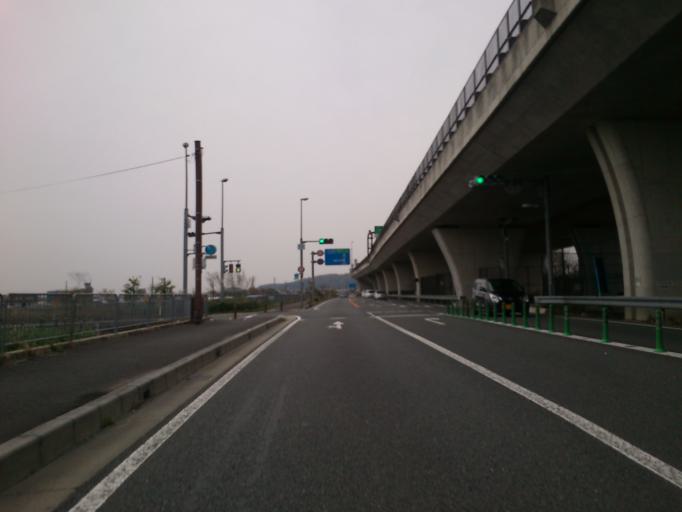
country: JP
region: Kyoto
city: Yawata
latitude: 34.8984
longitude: 135.7277
